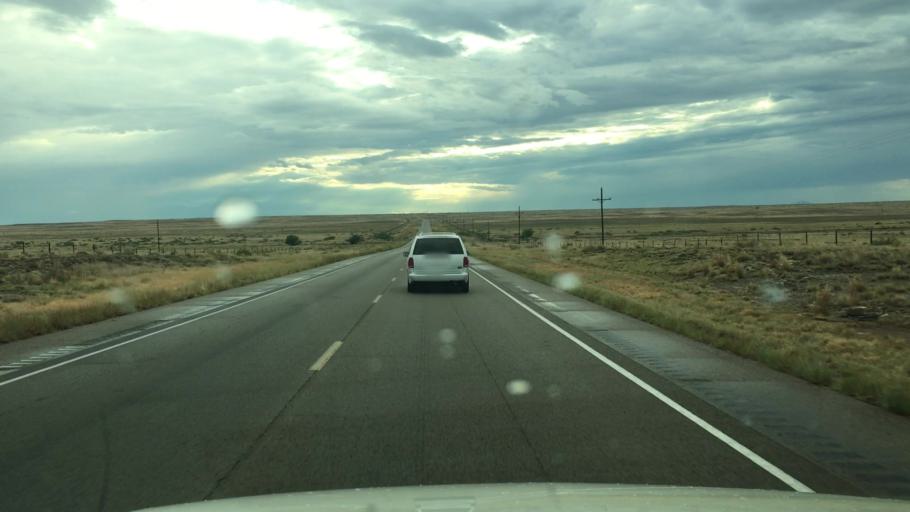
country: US
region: New Mexico
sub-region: Chaves County
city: Dexter
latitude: 33.4071
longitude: -104.2968
